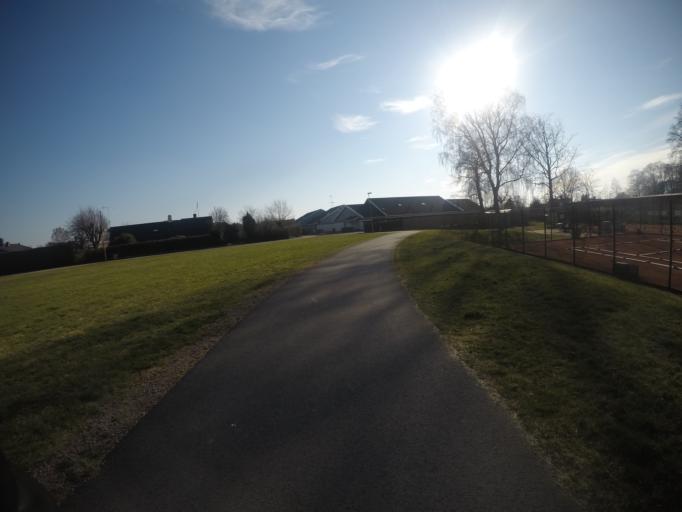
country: SE
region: Halland
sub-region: Laholms Kommun
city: Laholm
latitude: 56.5055
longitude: 13.0435
